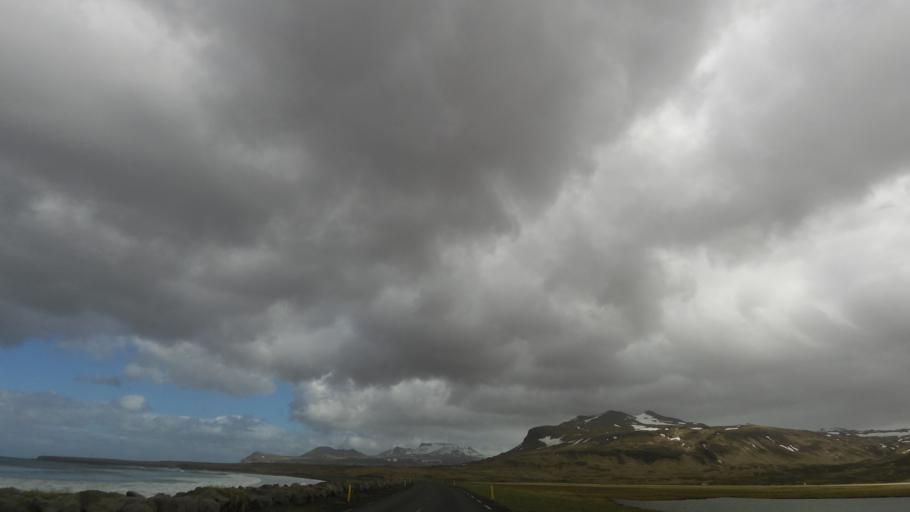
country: IS
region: West
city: Olafsvik
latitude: 64.8899
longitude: -23.6327
